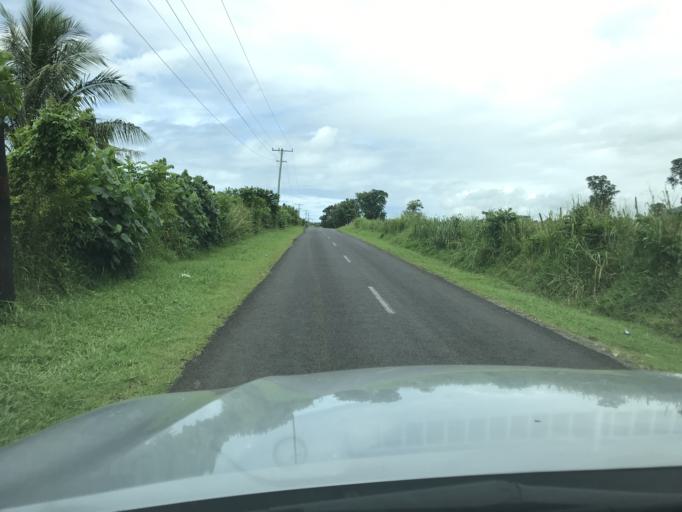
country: WS
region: A'ana
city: Leulumoega
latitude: -13.8771
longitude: -171.9367
